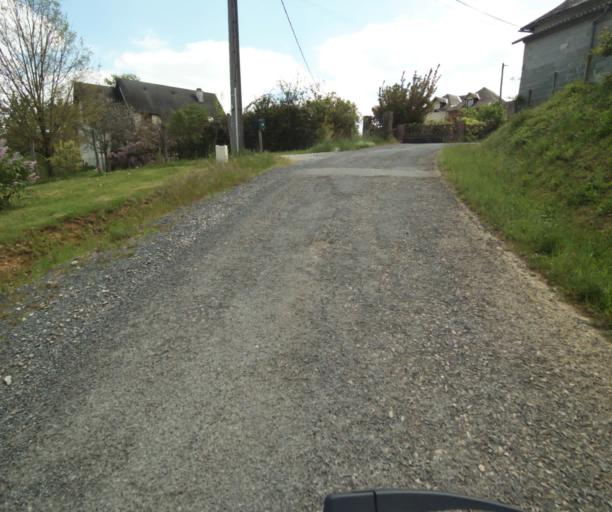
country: FR
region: Limousin
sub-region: Departement de la Correze
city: Tulle
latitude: 45.2732
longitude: 1.7606
